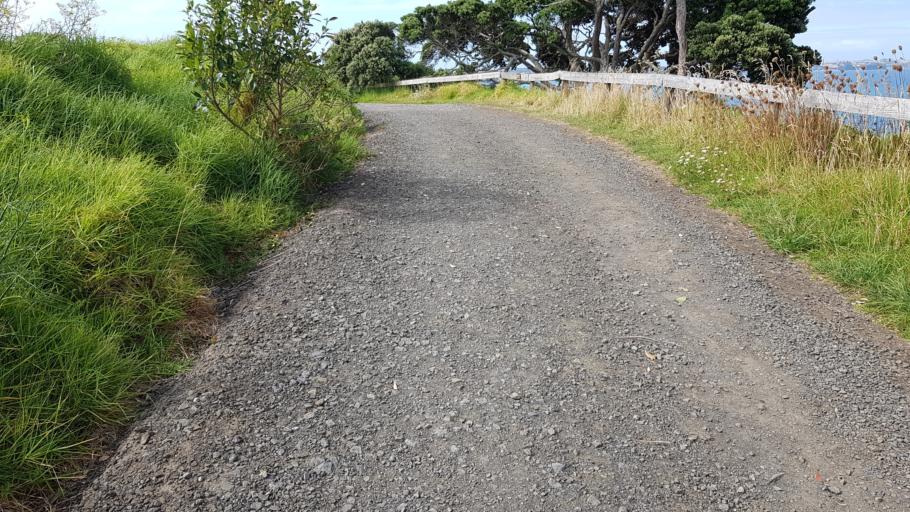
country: NZ
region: Auckland
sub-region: Auckland
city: Rothesay Bay
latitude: -36.6714
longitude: 174.7470
